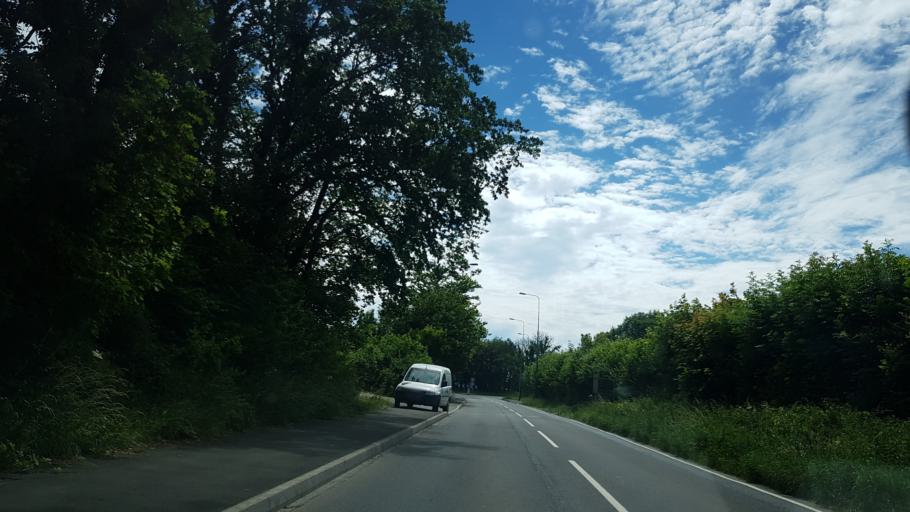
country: GB
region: Wales
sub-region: Pembrokeshire
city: Haverfordwest
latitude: 51.8173
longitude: -4.9556
